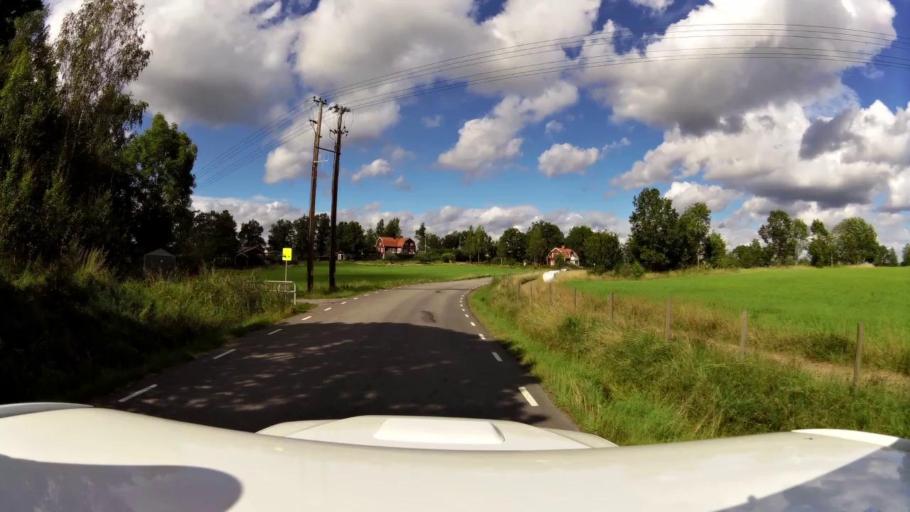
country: SE
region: OEstergoetland
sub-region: Kinda Kommun
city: Rimforsa
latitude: 58.2264
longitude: 15.6860
